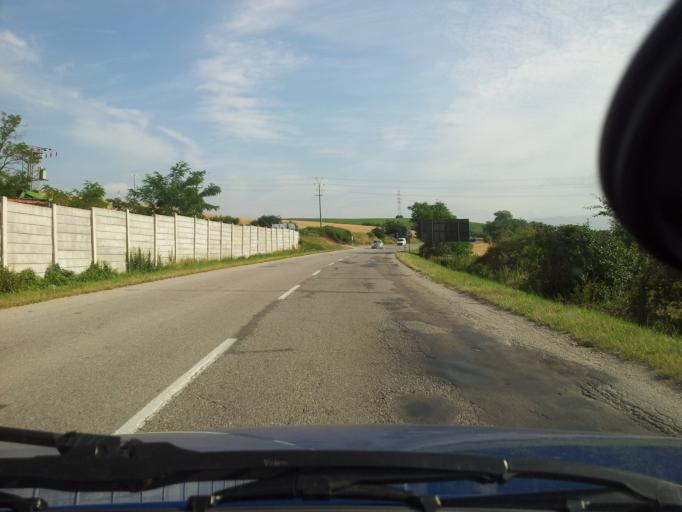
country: SK
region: Nitriansky
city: Partizanske
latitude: 48.6396
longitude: 18.3576
